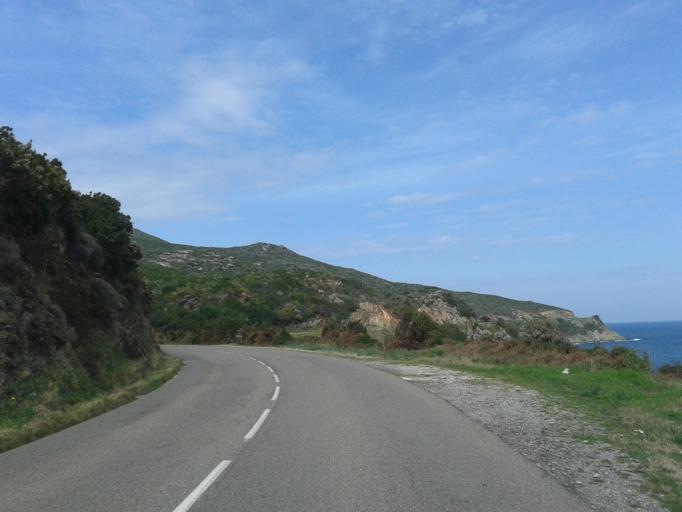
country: FR
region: Corsica
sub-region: Departement de la Haute-Corse
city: Brando
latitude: 42.8431
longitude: 9.4830
